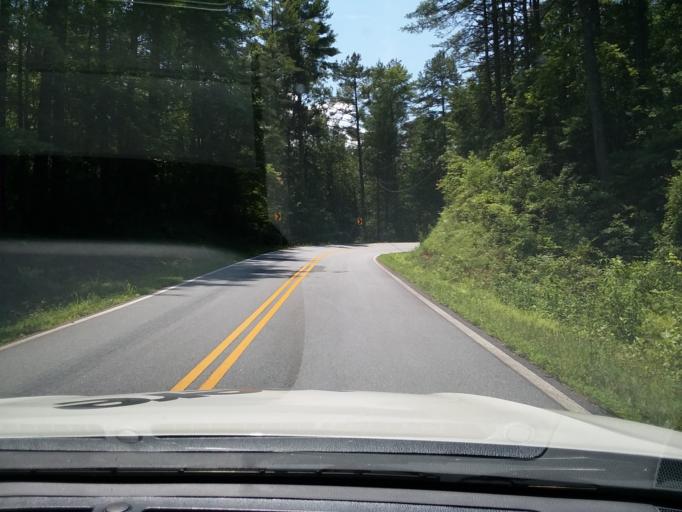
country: US
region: Georgia
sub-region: Rabun County
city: Mountain City
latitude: 34.9378
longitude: -83.1979
